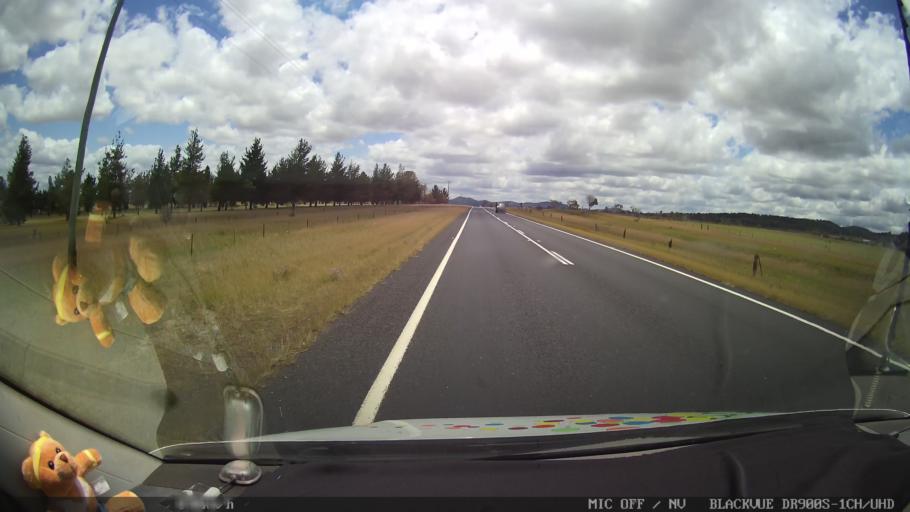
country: AU
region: New South Wales
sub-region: Glen Innes Severn
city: Glen Innes
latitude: -29.4304
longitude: 151.8553
